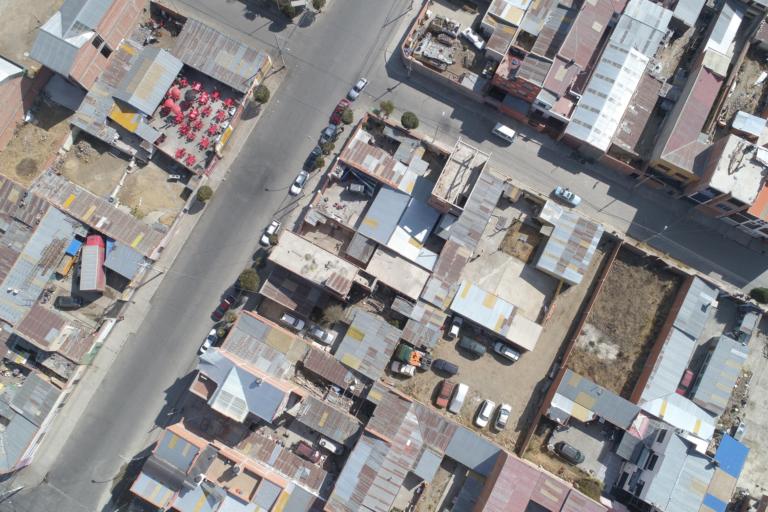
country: BO
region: La Paz
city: La Paz
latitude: -16.5278
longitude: -68.1470
